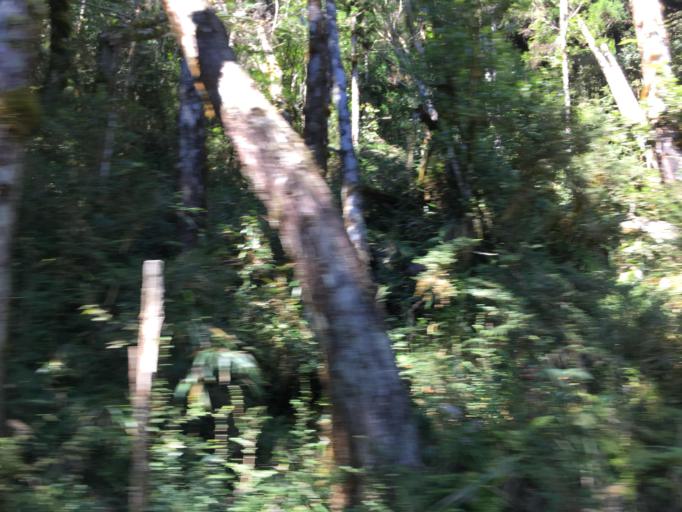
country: TW
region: Taiwan
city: Daxi
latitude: 24.5528
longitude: 121.3966
